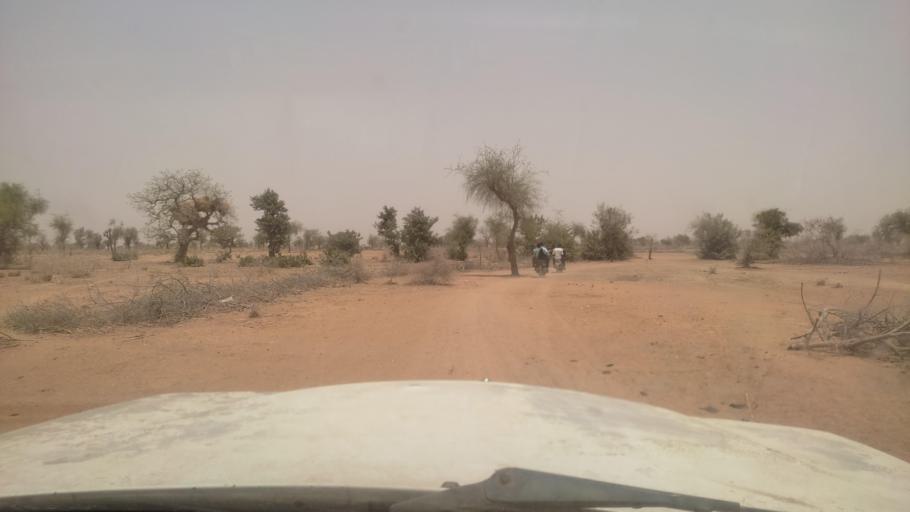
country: BF
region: Est
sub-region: Gnagna Province
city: Bogande
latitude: 13.0386
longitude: -0.0704
